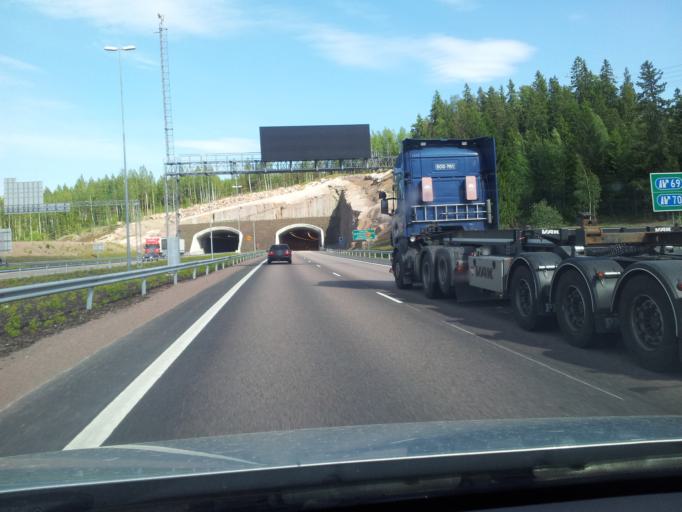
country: FI
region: Uusimaa
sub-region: Loviisa
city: Ruotsinpyhtaeae
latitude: 60.4929
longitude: 26.4324
